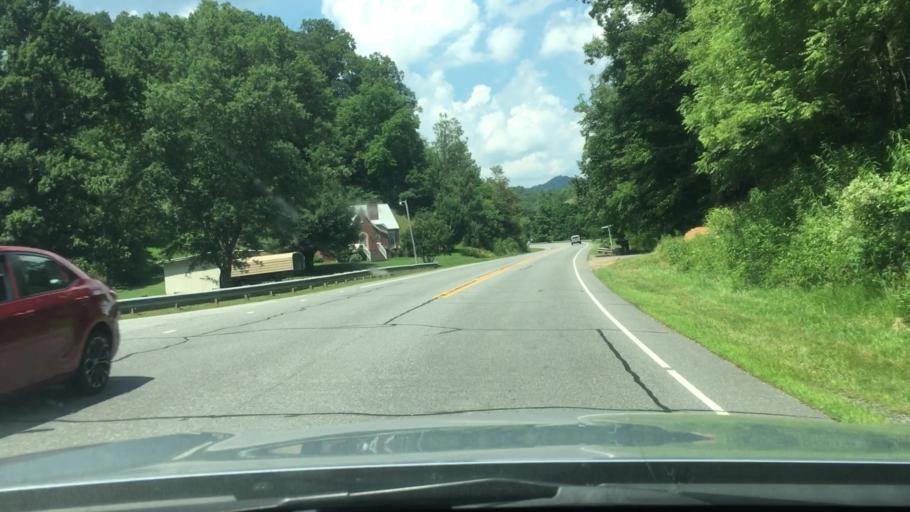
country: US
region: North Carolina
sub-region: Madison County
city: Marshall
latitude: 35.8102
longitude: -82.6570
